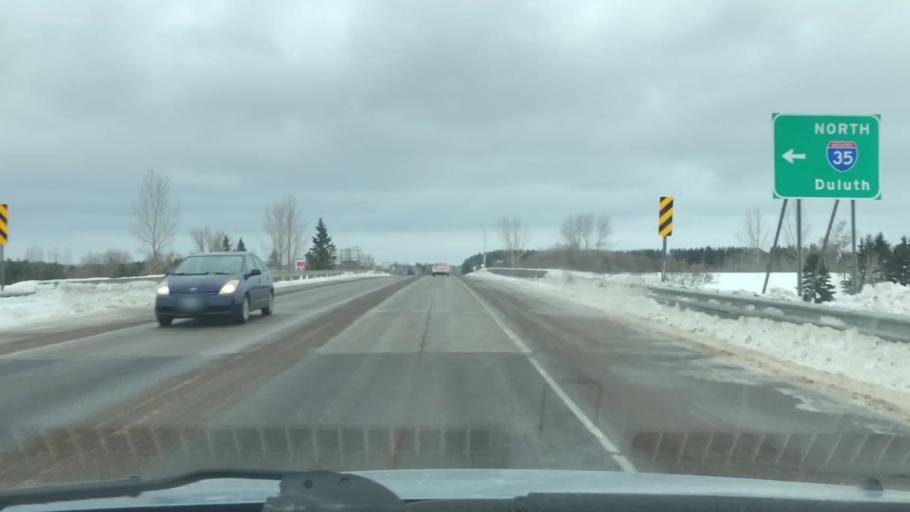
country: US
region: Minnesota
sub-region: Carlton County
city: Esko
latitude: 46.6970
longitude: -92.3652
